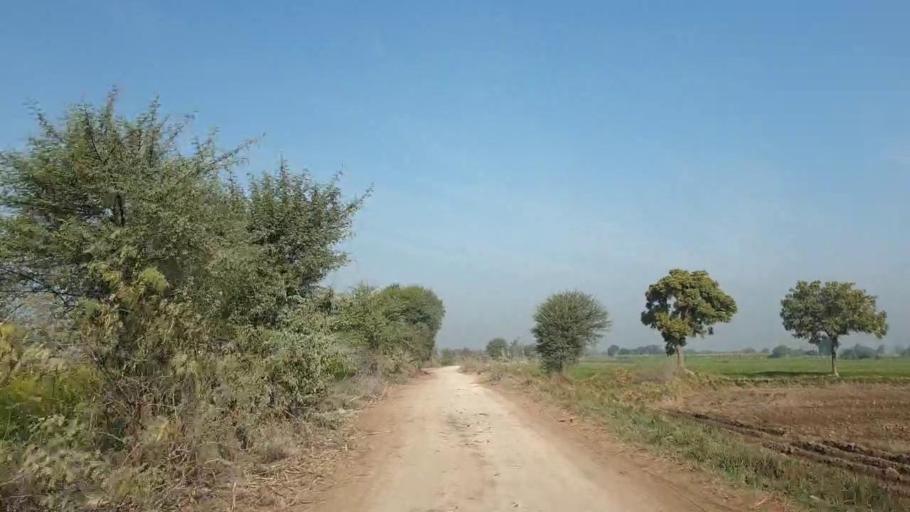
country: PK
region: Sindh
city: Tando Allahyar
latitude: 25.5774
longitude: 68.7145
